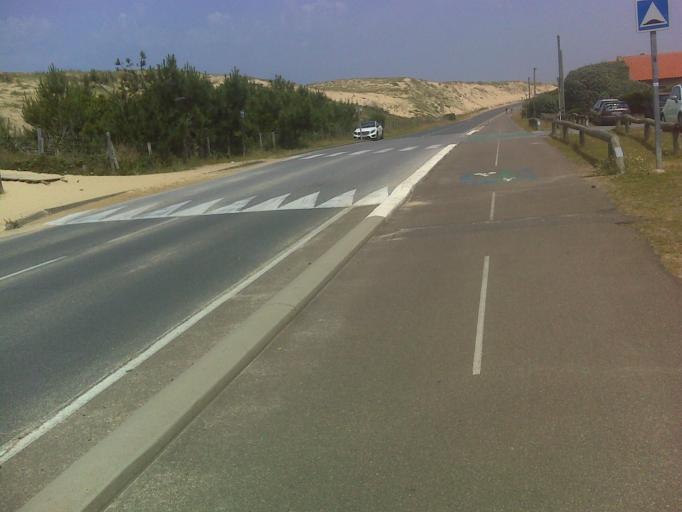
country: FR
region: Aquitaine
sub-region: Departement des Landes
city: Capbreton
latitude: 43.6770
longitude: -1.4379
